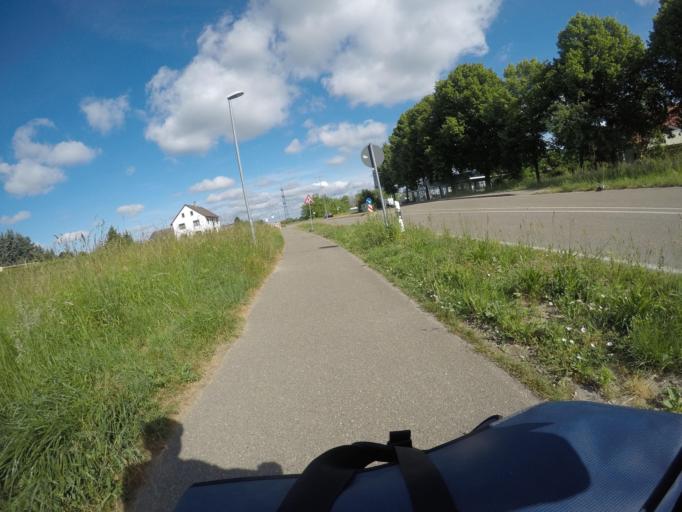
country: DE
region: Baden-Wuerttemberg
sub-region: Karlsruhe Region
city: Au am Rhein
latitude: 48.9448
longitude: 8.2470
